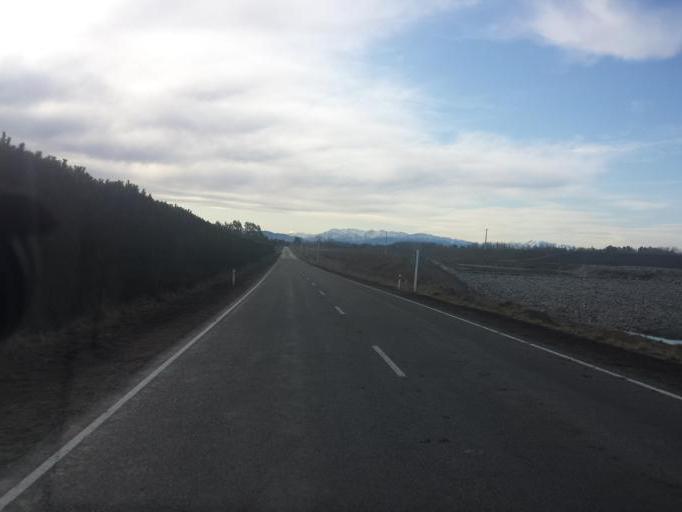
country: NZ
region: Canterbury
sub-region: Timaru District
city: Pleasant Point
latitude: -43.9927
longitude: 171.2958
